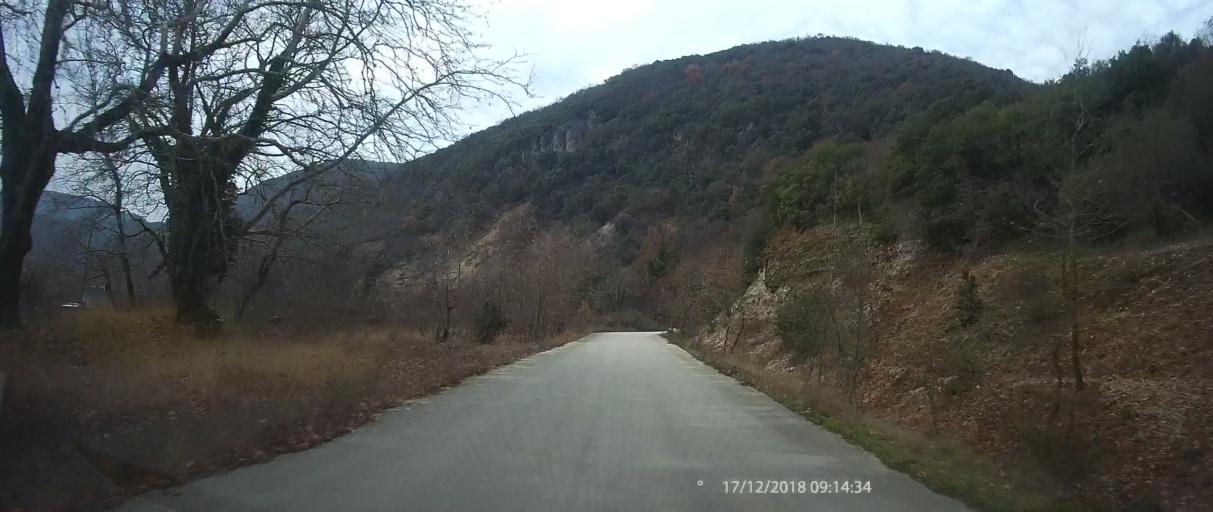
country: GR
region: Epirus
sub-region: Nomos Ioanninon
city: Kalpaki
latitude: 39.9721
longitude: 20.6552
